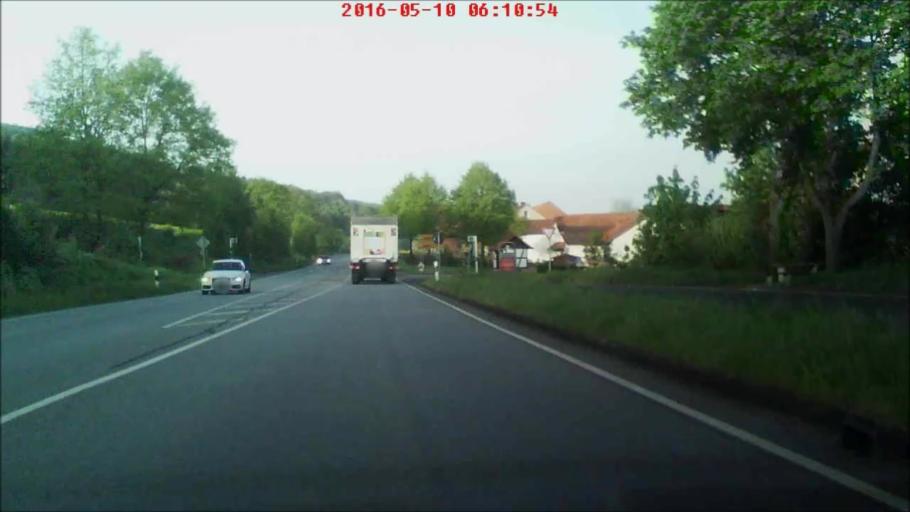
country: DE
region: Hesse
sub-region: Regierungsbezirk Kassel
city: Bad Hersfeld
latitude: 50.7886
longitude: 9.7160
